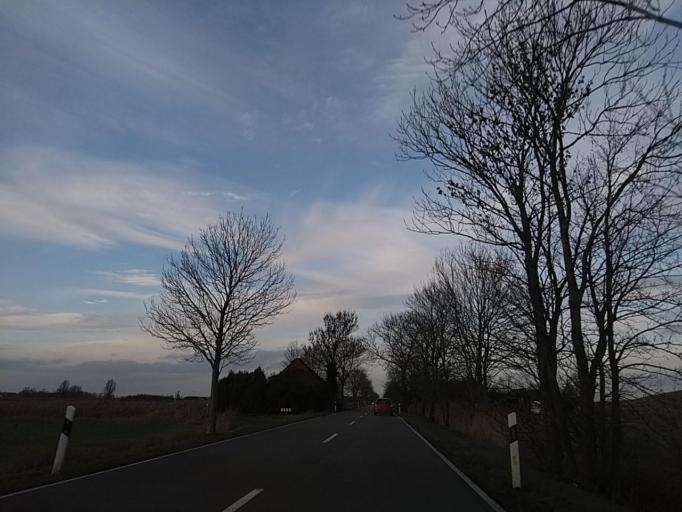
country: DE
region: Lower Saxony
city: Jemgum
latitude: 53.2407
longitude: 7.3922
